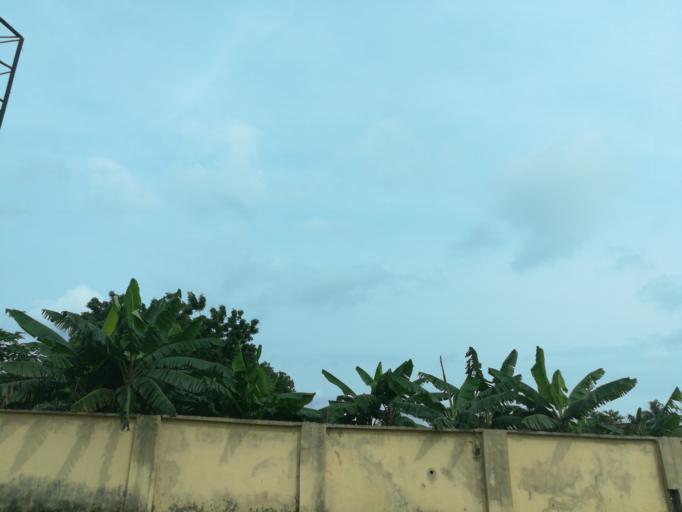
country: NG
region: Lagos
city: Oshodi
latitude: 6.5719
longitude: 3.3335
